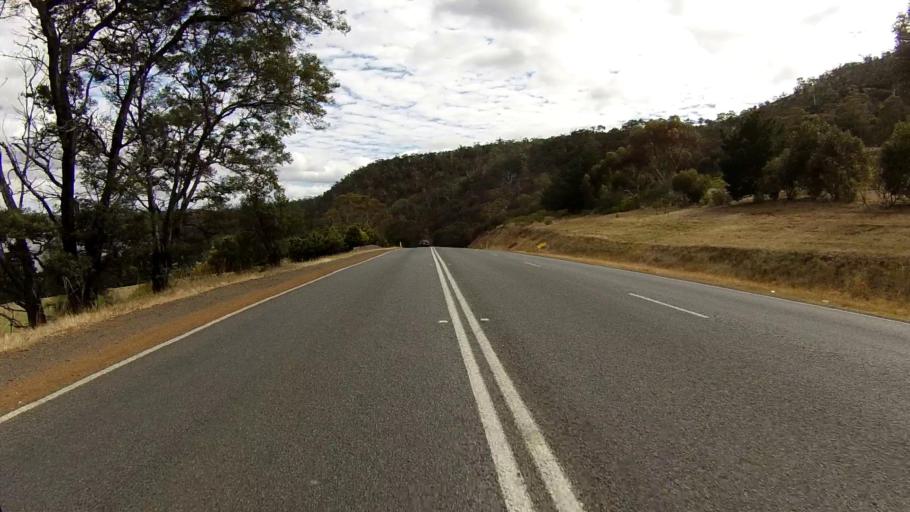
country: AU
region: Tasmania
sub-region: Brighton
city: Old Beach
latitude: -42.7932
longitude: 147.2929
